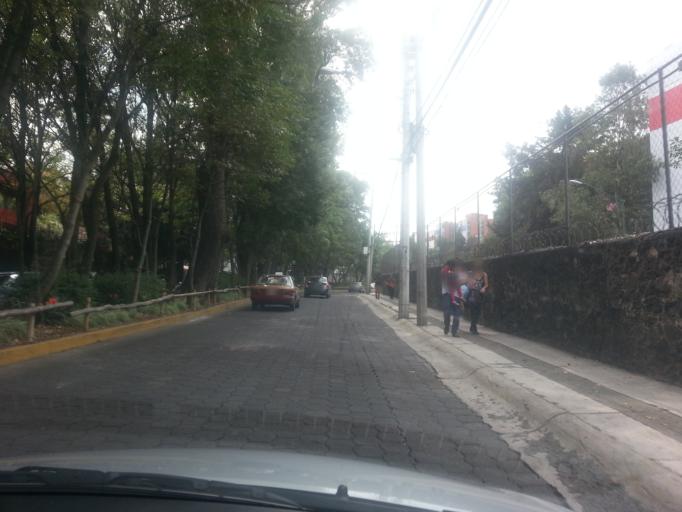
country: MX
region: Mexico City
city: Tlalpan
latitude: 19.2960
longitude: -99.1872
